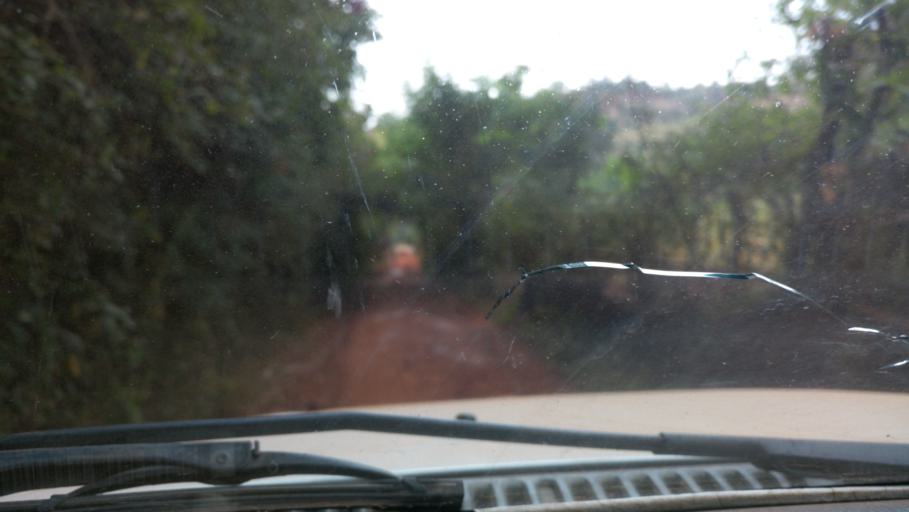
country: KE
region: Murang'a District
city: Maragua
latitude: -0.7703
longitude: 37.0957
